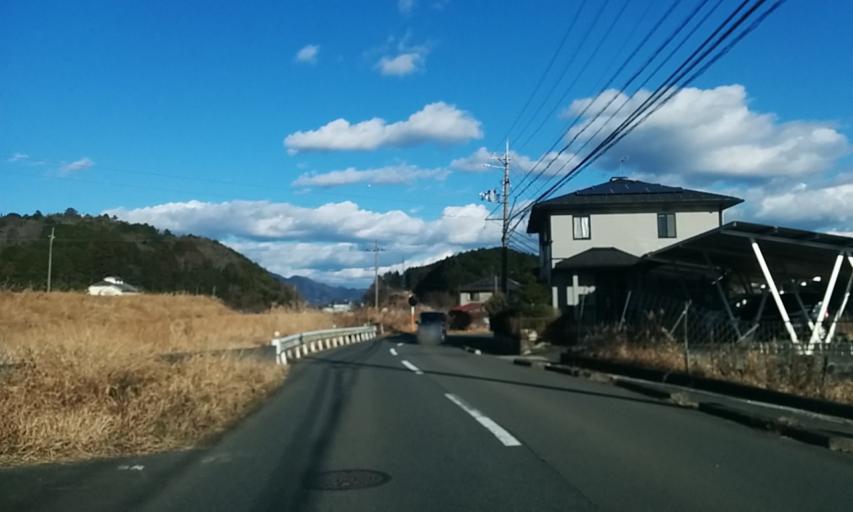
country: JP
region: Kyoto
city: Fukuchiyama
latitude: 35.2861
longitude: 135.0625
